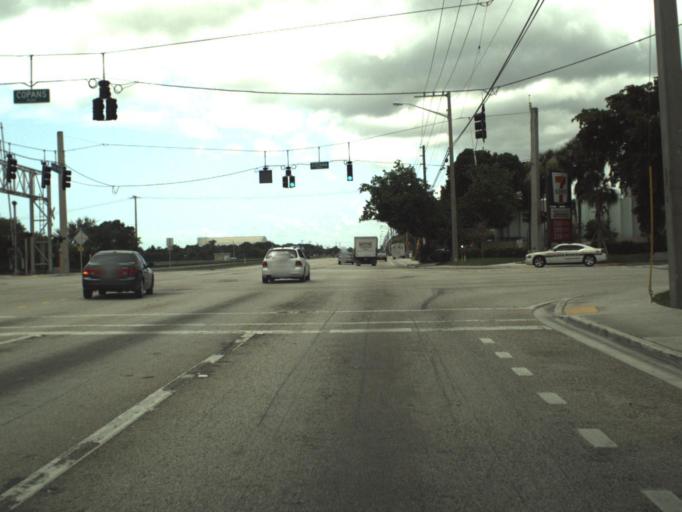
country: US
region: Florida
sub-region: Broward County
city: Kendall Green
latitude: 26.2609
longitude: -80.1179
